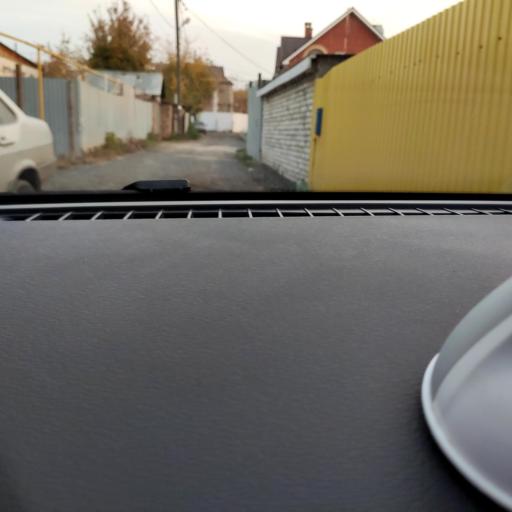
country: RU
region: Samara
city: Samara
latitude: 53.1821
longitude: 50.1234
